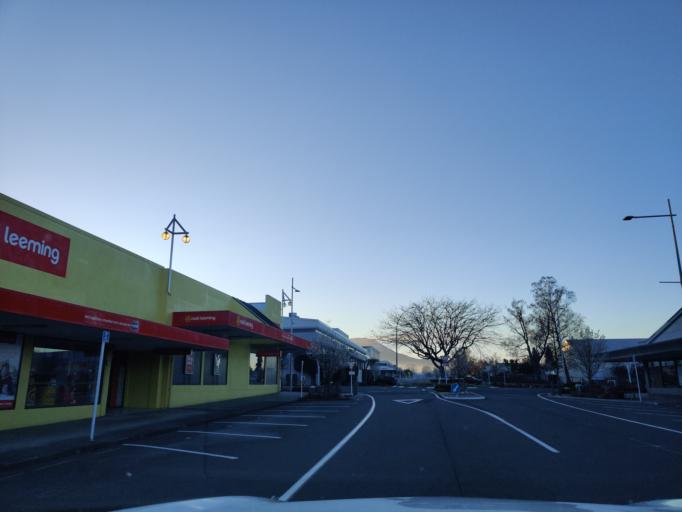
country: NZ
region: Waikato
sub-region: Taupo District
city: Taupo
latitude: -38.6860
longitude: 176.0719
